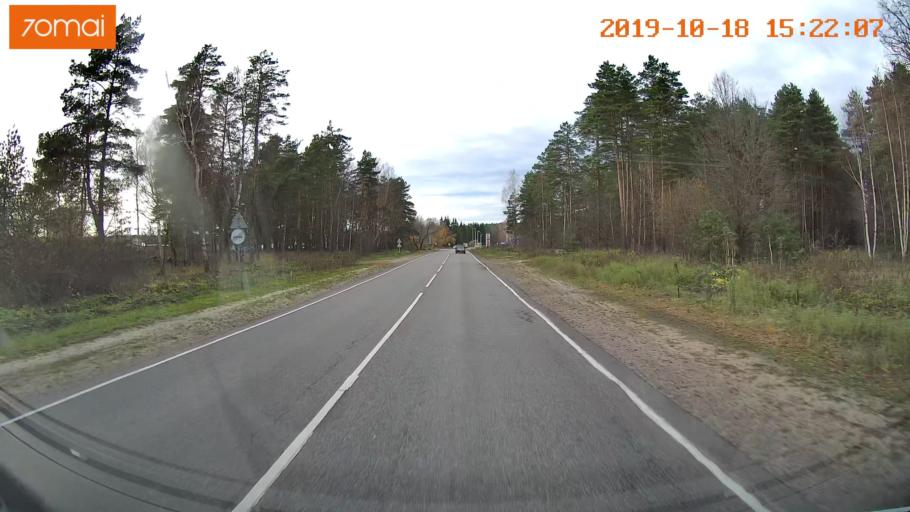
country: RU
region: Vladimir
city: Anopino
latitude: 55.7058
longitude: 40.7375
